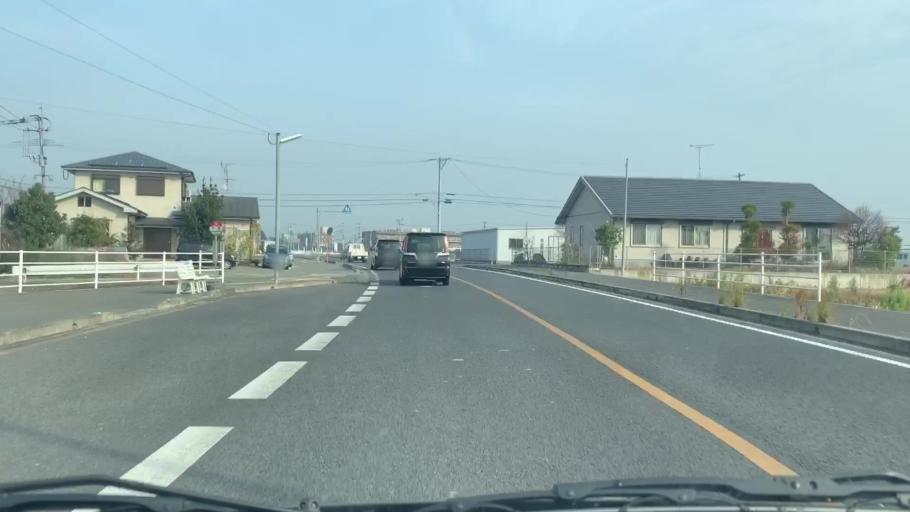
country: JP
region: Saga Prefecture
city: Saga-shi
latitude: 33.2357
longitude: 130.2578
